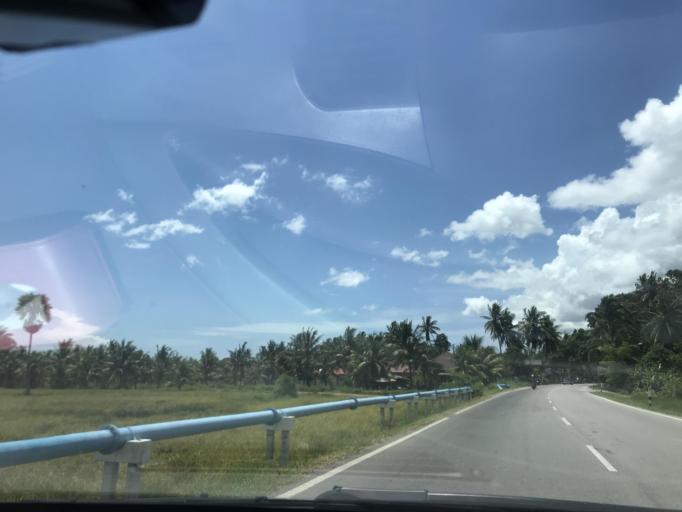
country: MY
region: Kelantan
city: Tumpat
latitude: 6.1947
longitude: 102.1401
